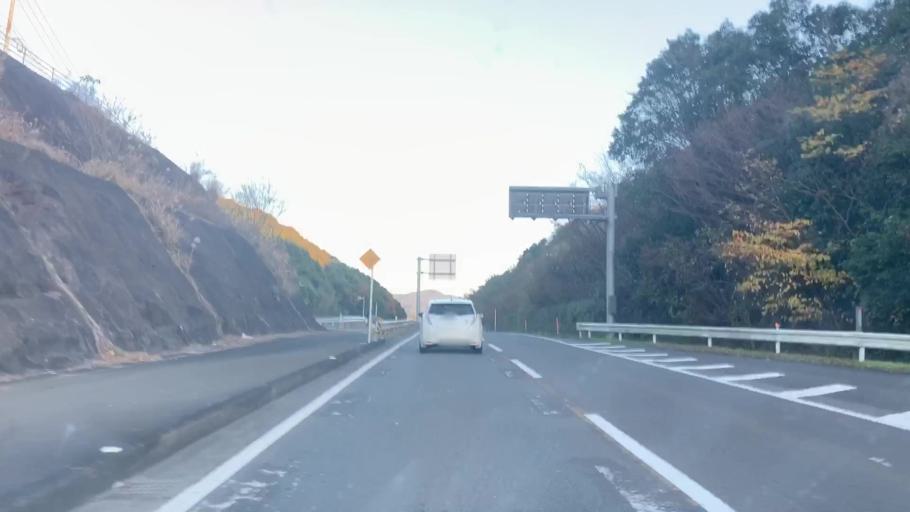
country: JP
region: Saga Prefecture
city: Imaricho-ko
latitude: 33.2631
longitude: 129.9680
